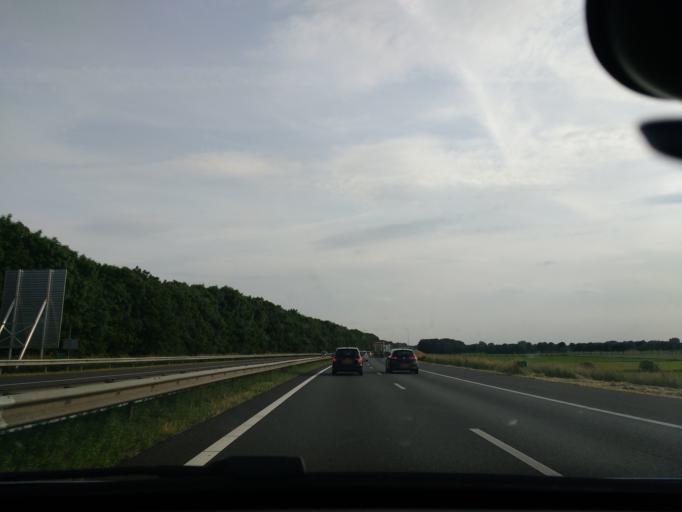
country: NL
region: Gelderland
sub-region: Gemeente Wijchen
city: Bergharen
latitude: 51.8041
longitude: 5.6750
